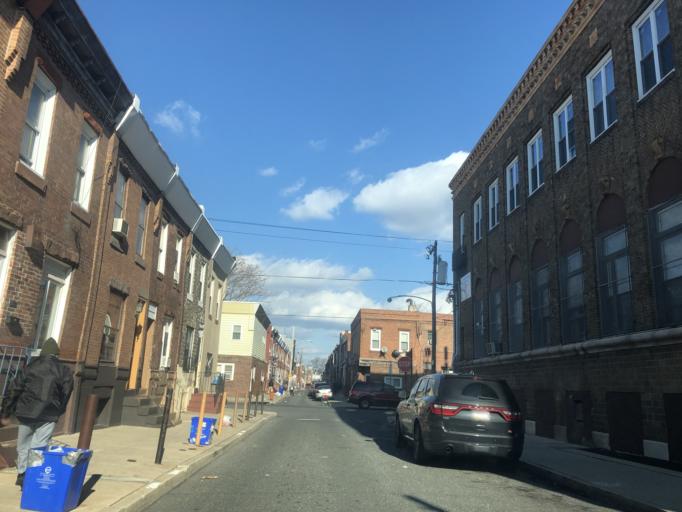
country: US
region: Pennsylvania
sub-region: Philadelphia County
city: Philadelphia
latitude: 39.9174
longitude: -75.1584
